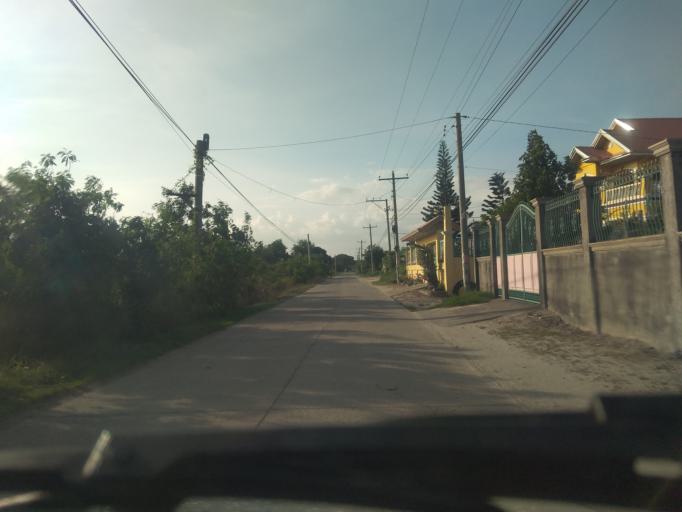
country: PH
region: Central Luzon
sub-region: Province of Pampanga
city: Mexico
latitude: 15.0823
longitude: 120.7014
